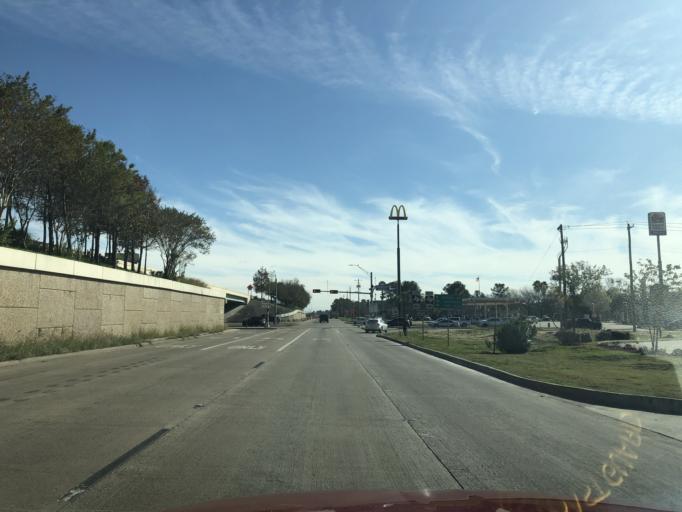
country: US
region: Texas
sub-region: Galveston County
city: Dickinson
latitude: 29.4497
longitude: -95.0779
